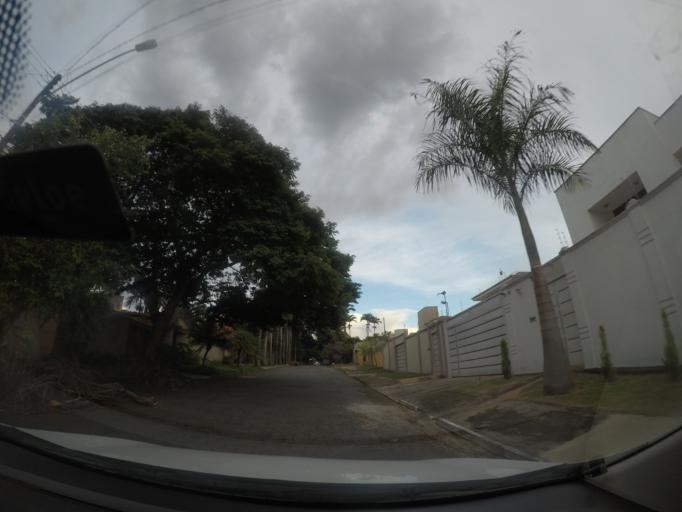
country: BR
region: Goias
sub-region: Goiania
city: Goiania
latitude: -16.6533
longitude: -49.2294
